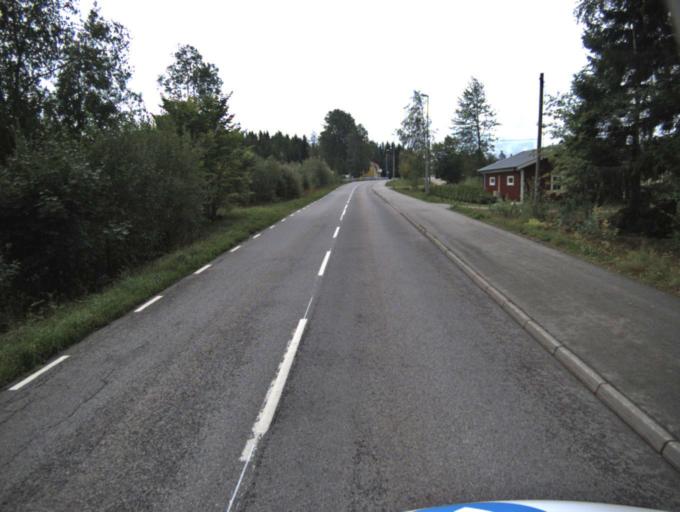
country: SE
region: Vaestra Goetaland
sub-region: Ulricehamns Kommun
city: Ulricehamn
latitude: 57.7754
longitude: 13.4313
